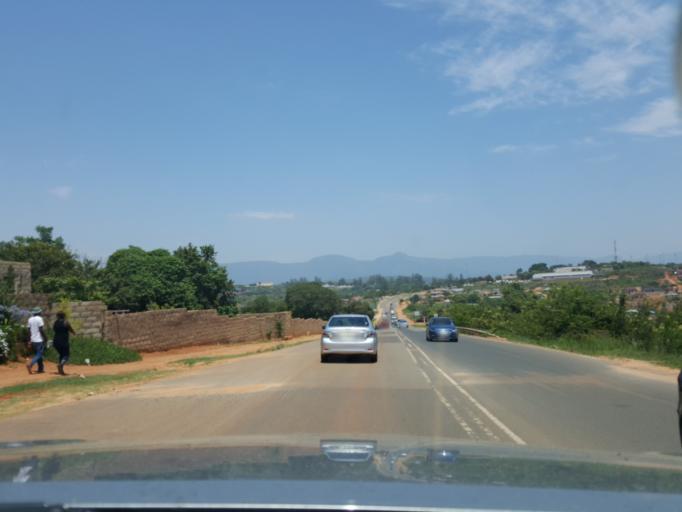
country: ZA
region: Limpopo
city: Thulamahashi
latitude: -24.8443
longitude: 31.0861
